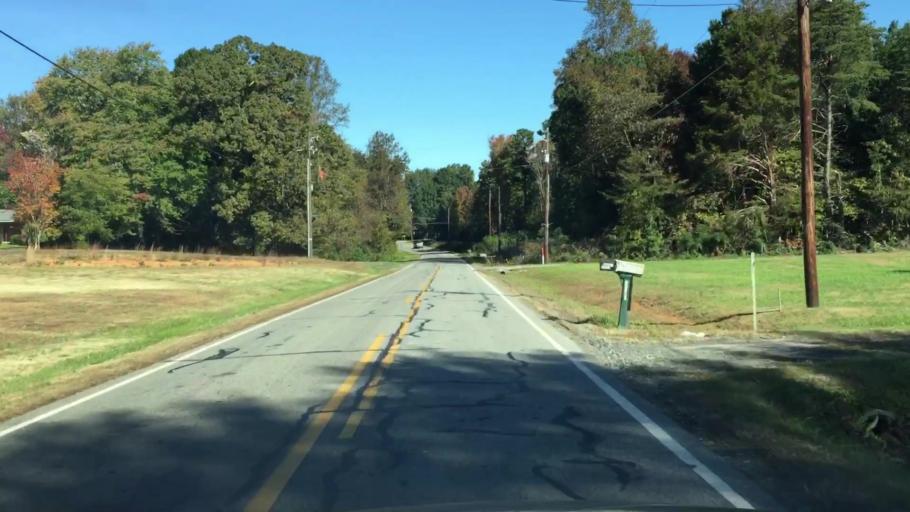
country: US
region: North Carolina
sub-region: Rockingham County
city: Reidsville
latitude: 36.3175
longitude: -79.6292
